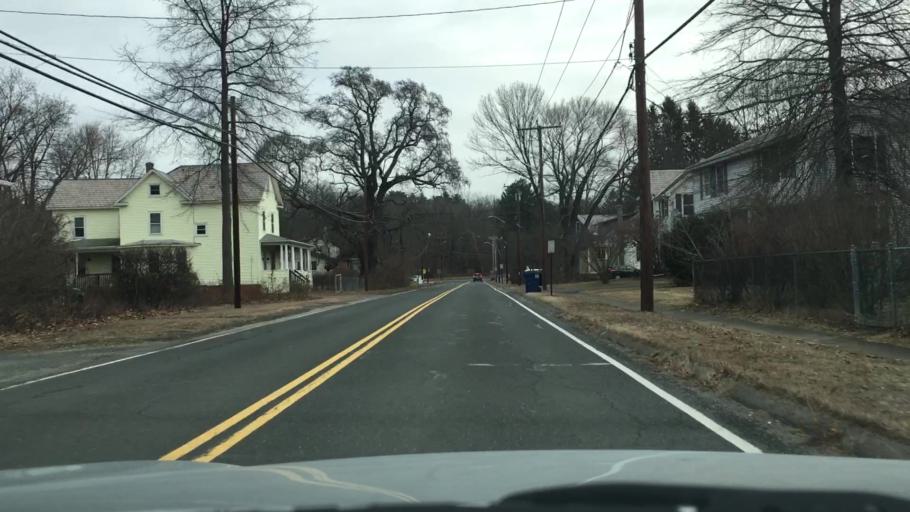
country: US
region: Massachusetts
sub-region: Hampshire County
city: Northampton
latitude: 42.3255
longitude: -72.6548
